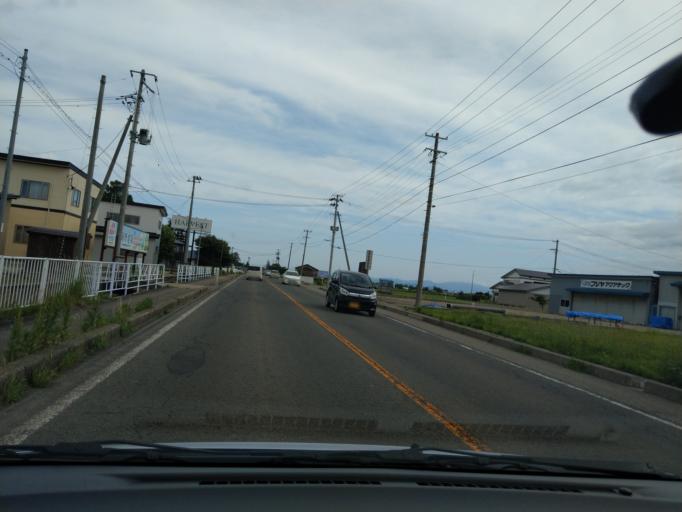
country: JP
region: Akita
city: Yokotemachi
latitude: 39.4038
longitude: 140.5601
